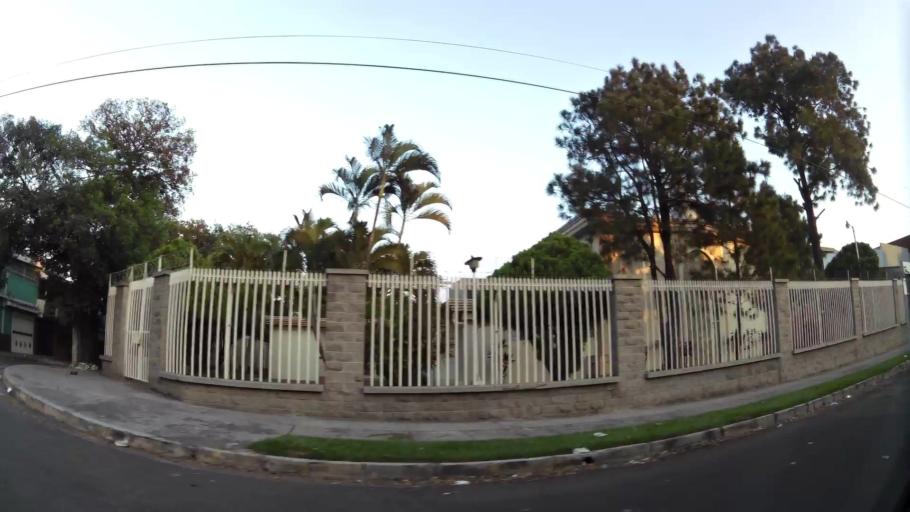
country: SV
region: San Salvador
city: Delgado
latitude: 13.7141
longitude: -89.1916
